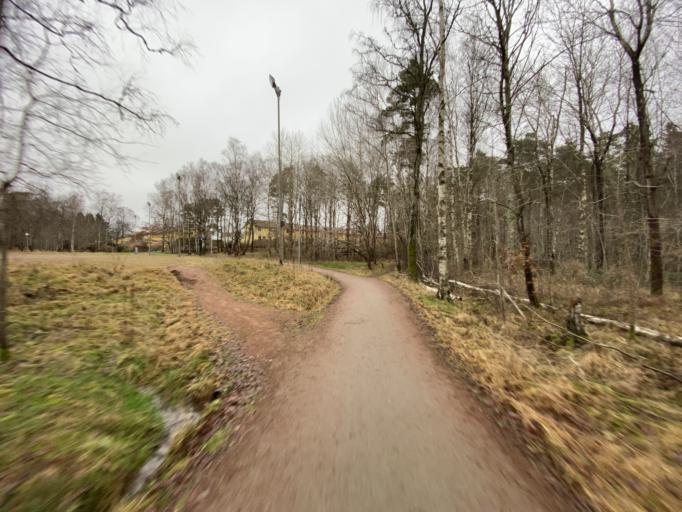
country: SE
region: Vaestra Goetaland
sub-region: Goteborg
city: Eriksbo
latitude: 57.7116
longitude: 12.0479
